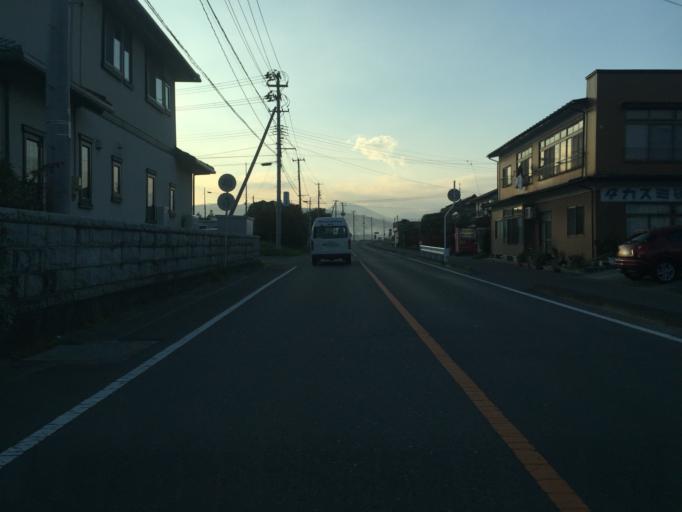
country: JP
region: Fukushima
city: Motomiya
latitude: 37.5228
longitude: 140.3878
